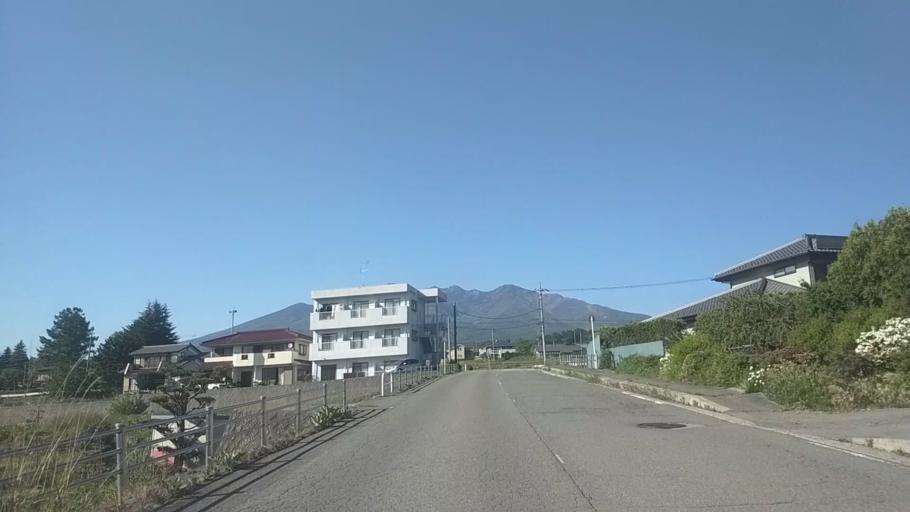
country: JP
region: Nagano
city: Chino
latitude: 35.8667
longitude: 138.3127
